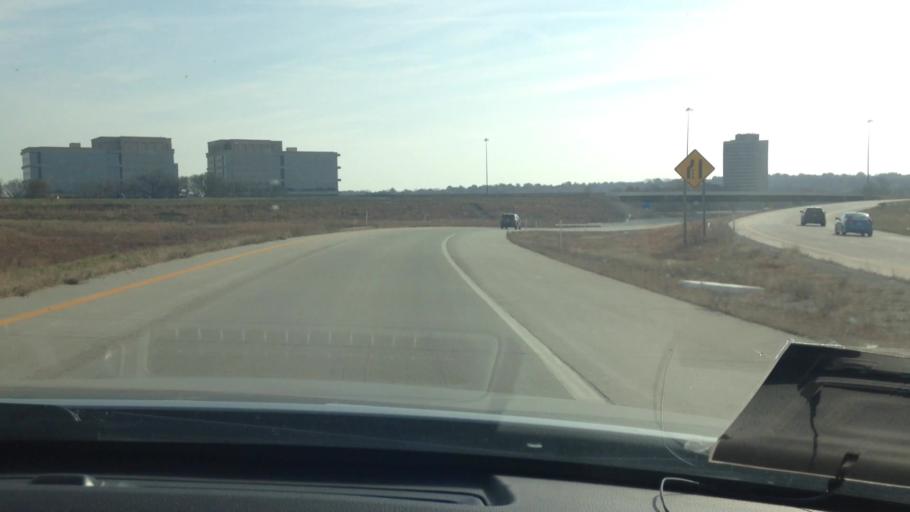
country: US
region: Kansas
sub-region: Johnson County
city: Lenexa
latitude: 38.9339
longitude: -94.7087
